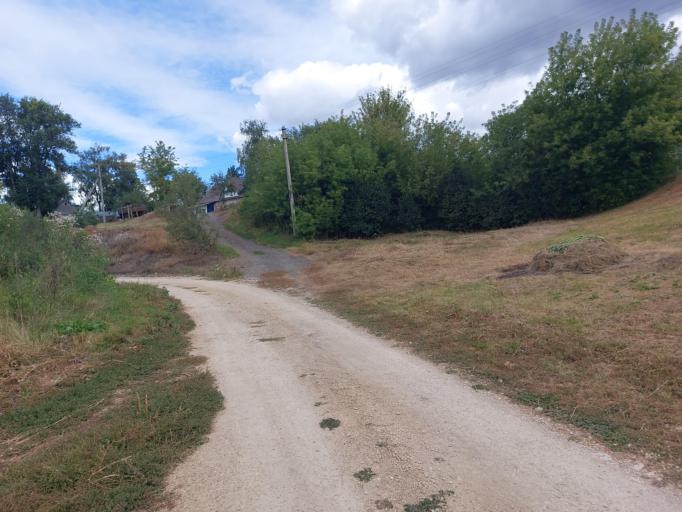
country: RU
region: Lipetsk
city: Terbuny
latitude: 52.2629
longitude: 38.2073
